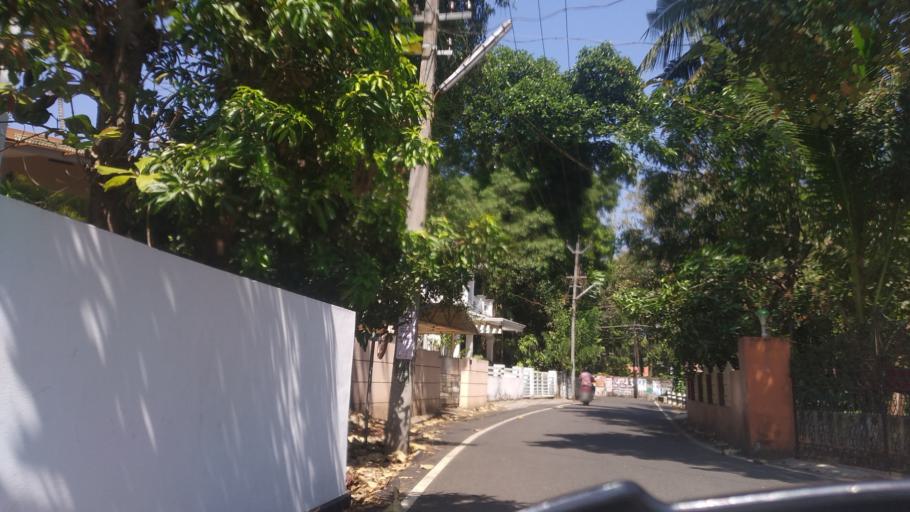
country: IN
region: Kerala
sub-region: Thrissur District
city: Kodungallur
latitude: 10.1364
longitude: 76.2252
